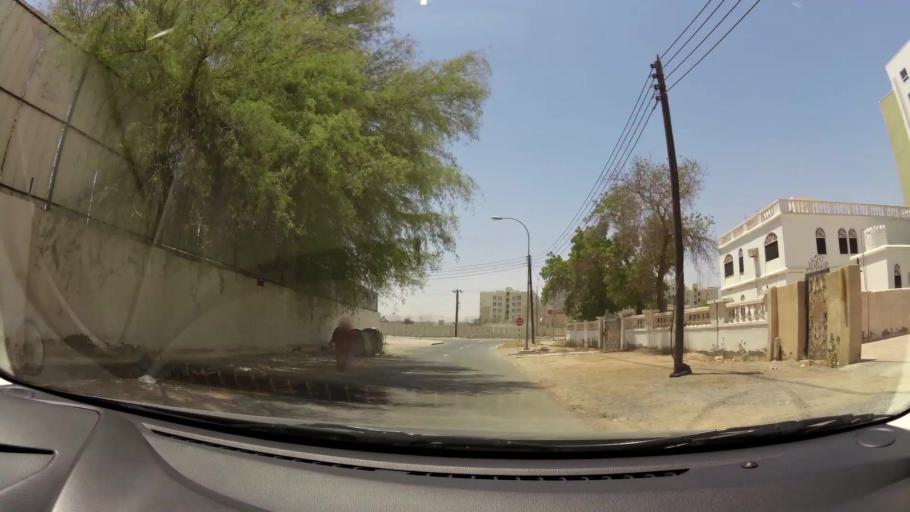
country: OM
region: Muhafazat Masqat
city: As Sib al Jadidah
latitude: 23.6227
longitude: 58.2430
